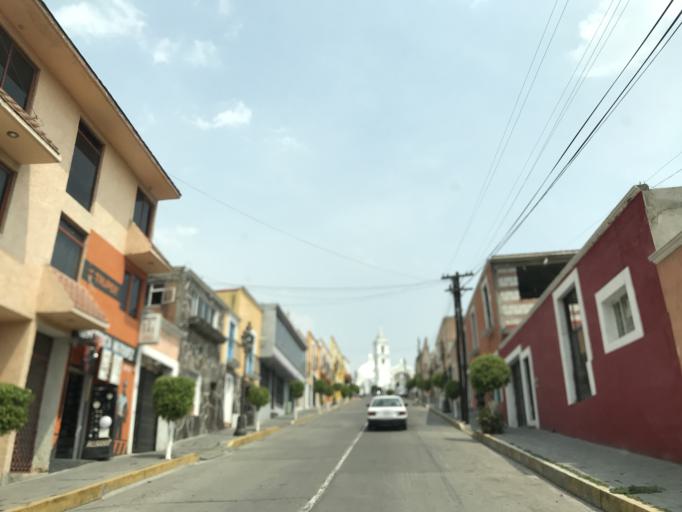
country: MX
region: Tlaxcala
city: Panotla
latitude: 19.3158
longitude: -98.2684
